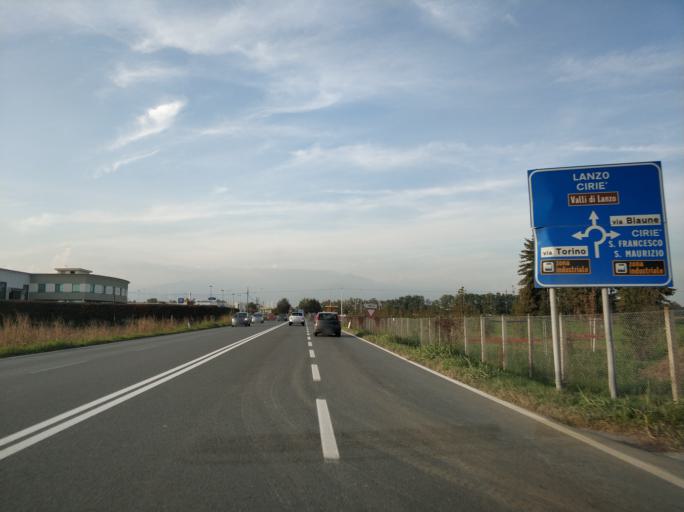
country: IT
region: Piedmont
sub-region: Provincia di Torino
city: San Maurizio
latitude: 45.2136
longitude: 7.6137
